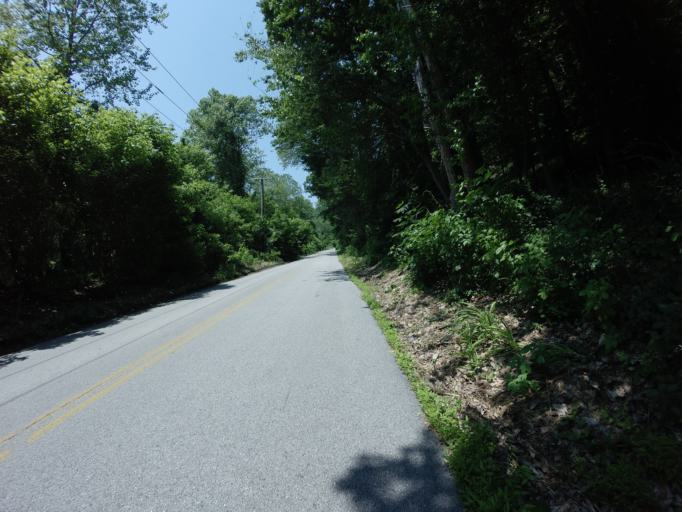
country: US
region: Maryland
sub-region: Howard County
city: Ilchester
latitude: 39.2570
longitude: -76.7756
